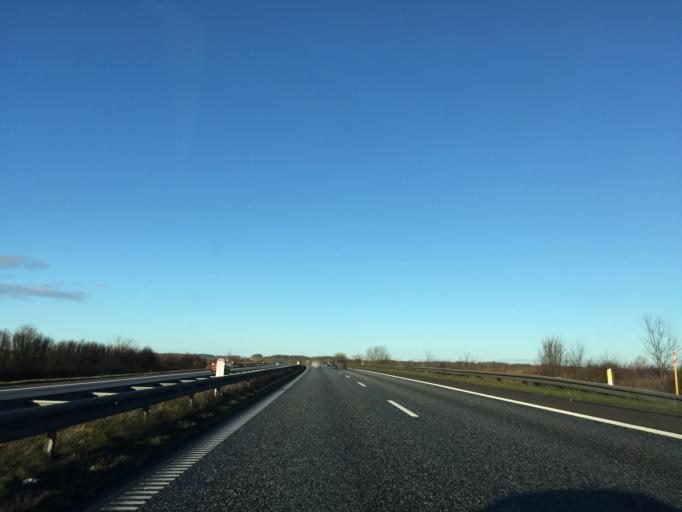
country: DK
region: South Denmark
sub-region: Fredericia Kommune
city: Taulov
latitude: 55.5759
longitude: 9.6147
